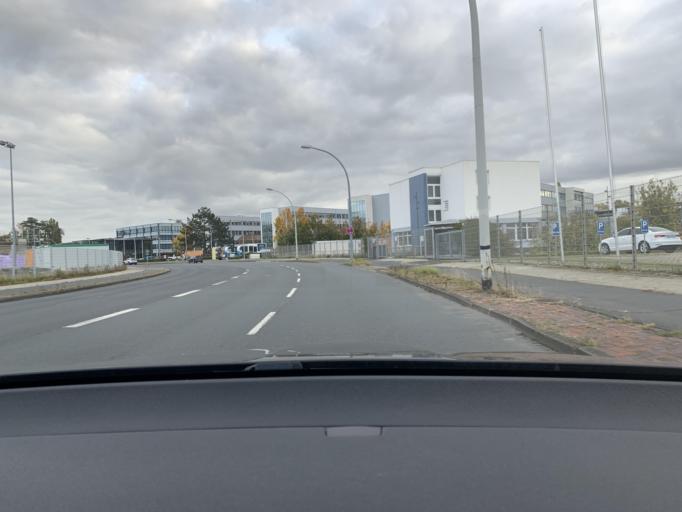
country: DE
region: Lower Saxony
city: Braunschweig
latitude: 52.2978
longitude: 10.5128
